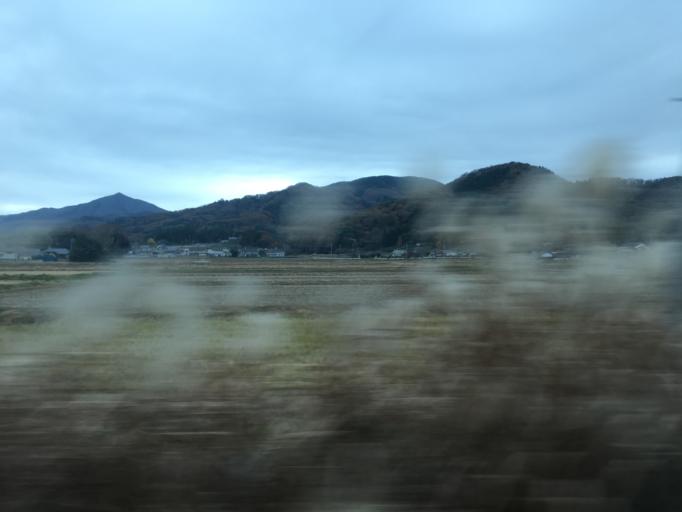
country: JP
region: Ibaraki
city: Iwase
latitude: 36.3570
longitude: 140.1288
